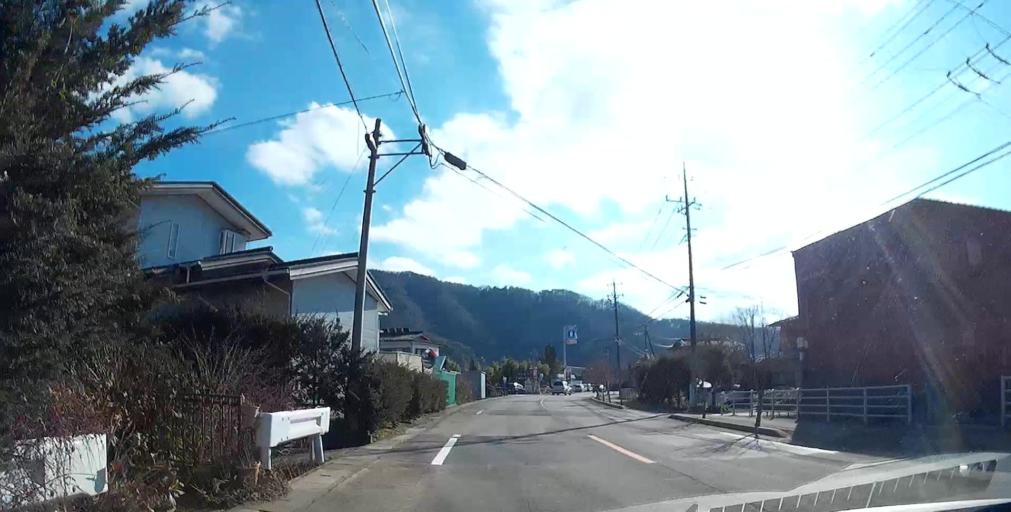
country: JP
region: Yamanashi
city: Fujikawaguchiko
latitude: 35.5246
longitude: 138.7740
